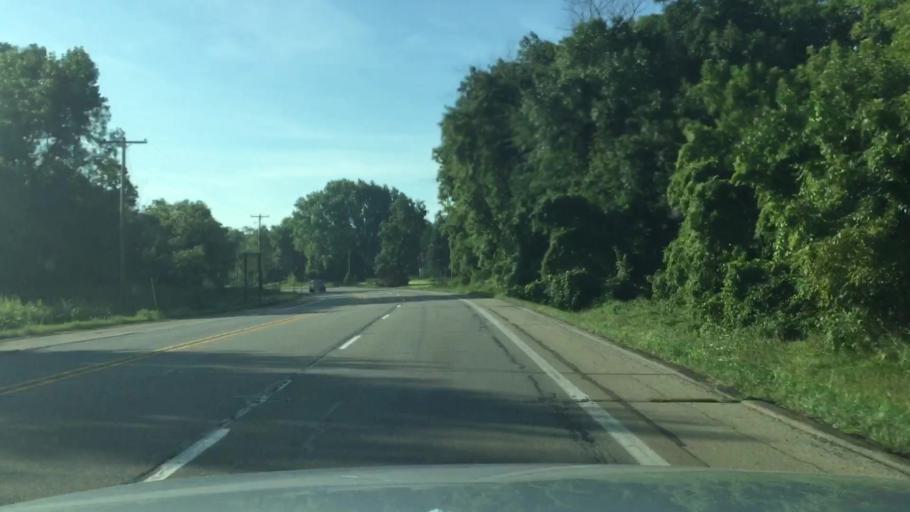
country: US
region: Michigan
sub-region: Lenawee County
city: Manitou Beach-Devils Lake
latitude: 42.0461
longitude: -84.3574
